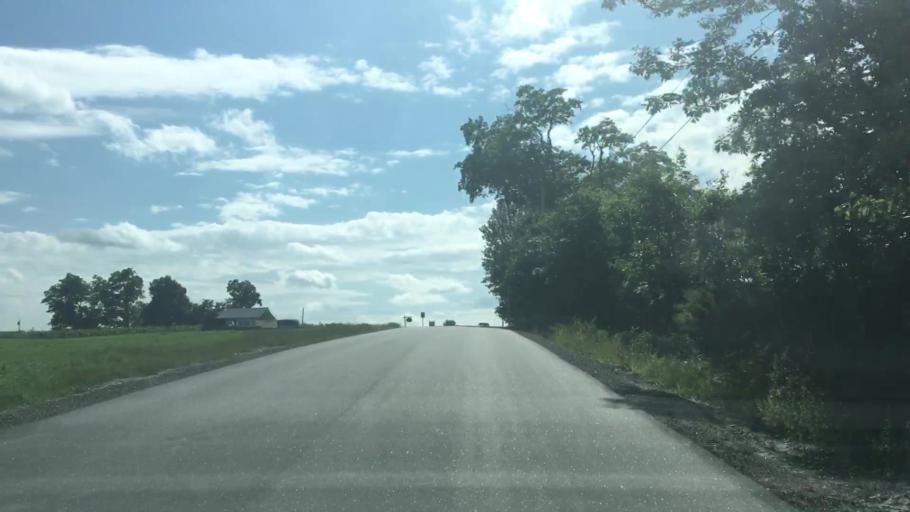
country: US
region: Maine
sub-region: Androscoggin County
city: Poland
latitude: 44.0057
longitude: -70.3706
